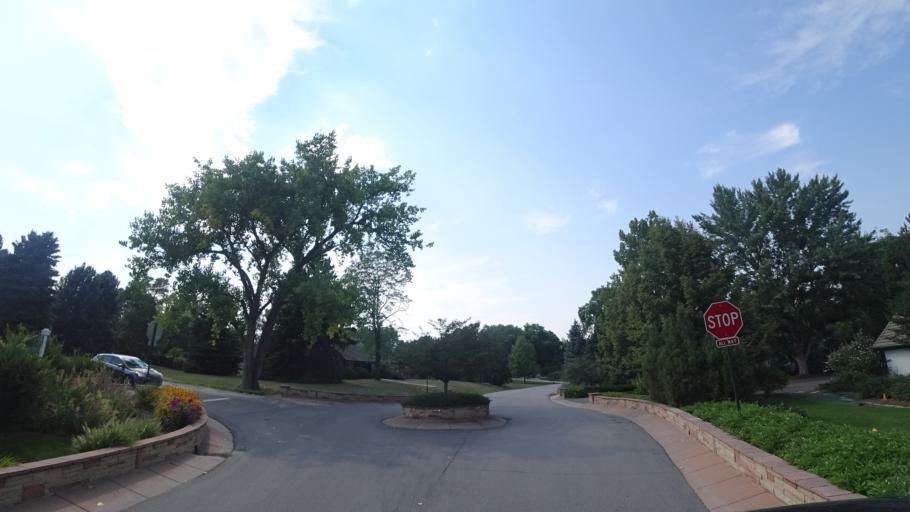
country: US
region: Colorado
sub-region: Arapahoe County
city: Greenwood Village
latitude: 39.6155
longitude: -104.9652
